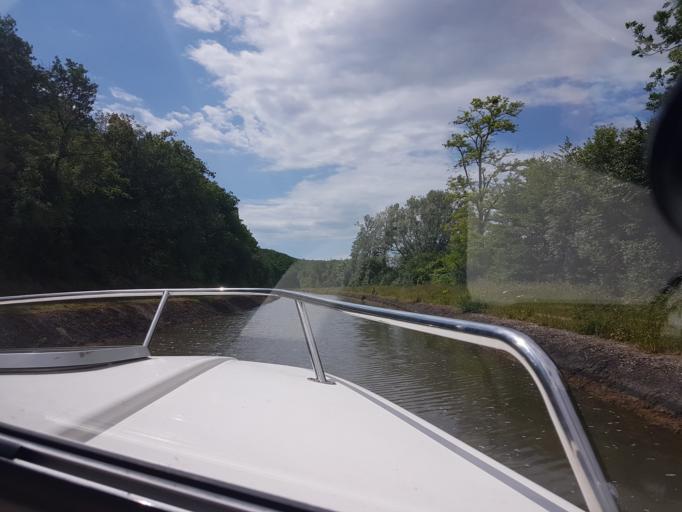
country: FR
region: Bourgogne
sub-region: Departement de la Nievre
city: Clamecy
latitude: 47.5079
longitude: 3.5209
